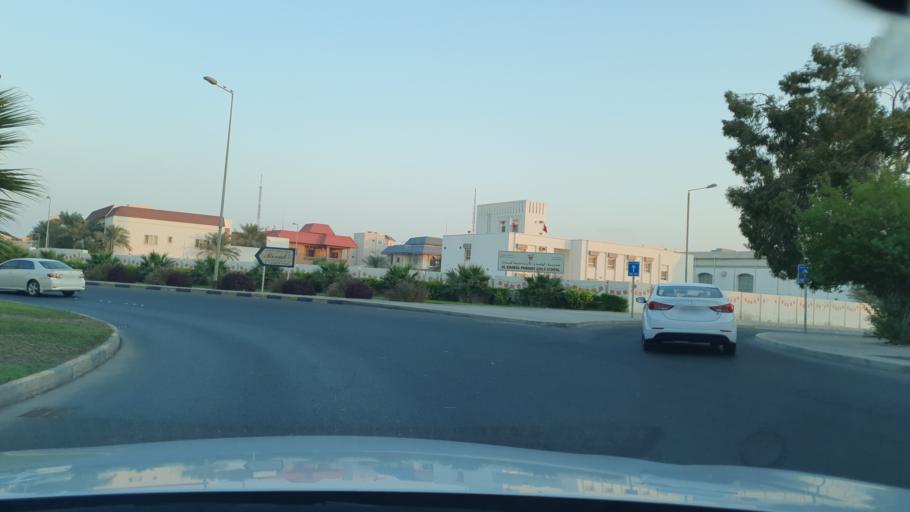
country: BH
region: Northern
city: Madinat `Isa
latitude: 26.1701
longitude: 50.5482
